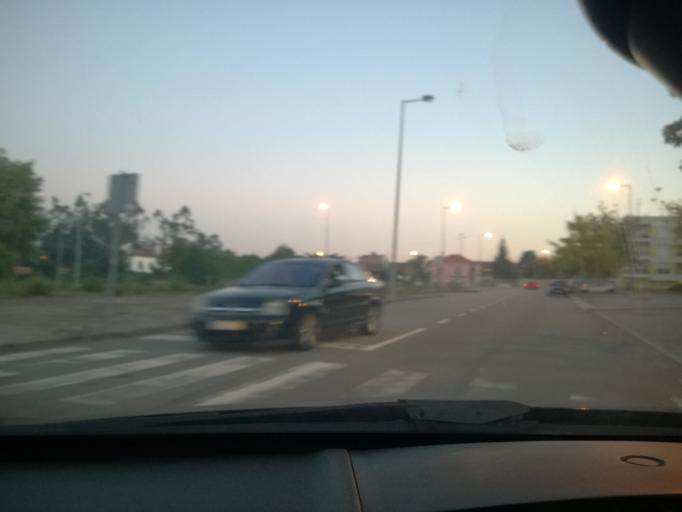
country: PT
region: Porto
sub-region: Maia
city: Anta
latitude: 41.2624
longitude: -8.6146
